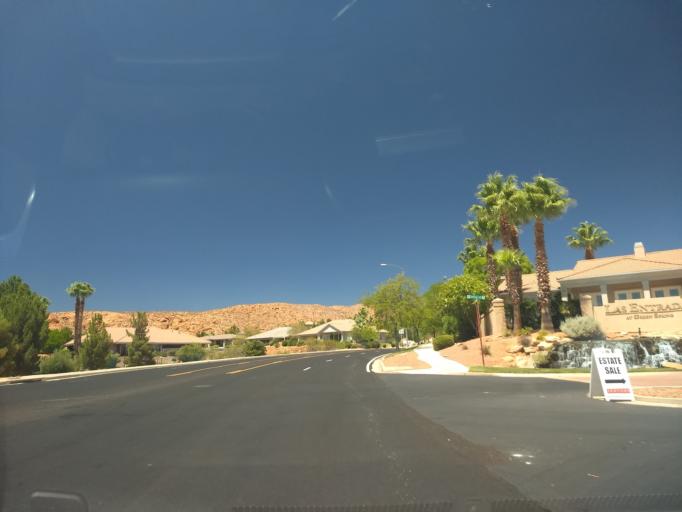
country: US
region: Utah
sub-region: Washington County
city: Washington
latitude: 37.1406
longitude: -113.5281
